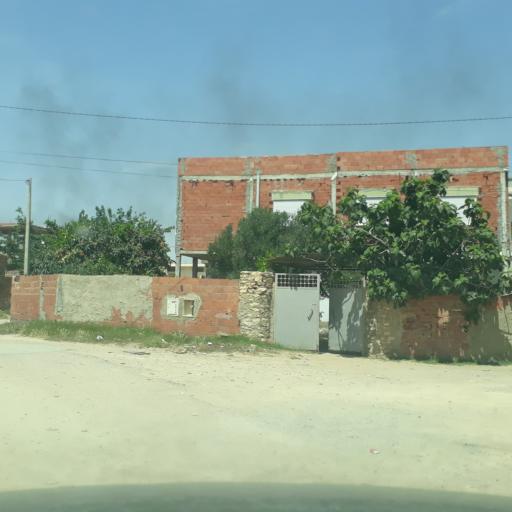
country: TN
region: Safaqis
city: Al Qarmadah
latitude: 34.8233
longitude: 10.7787
